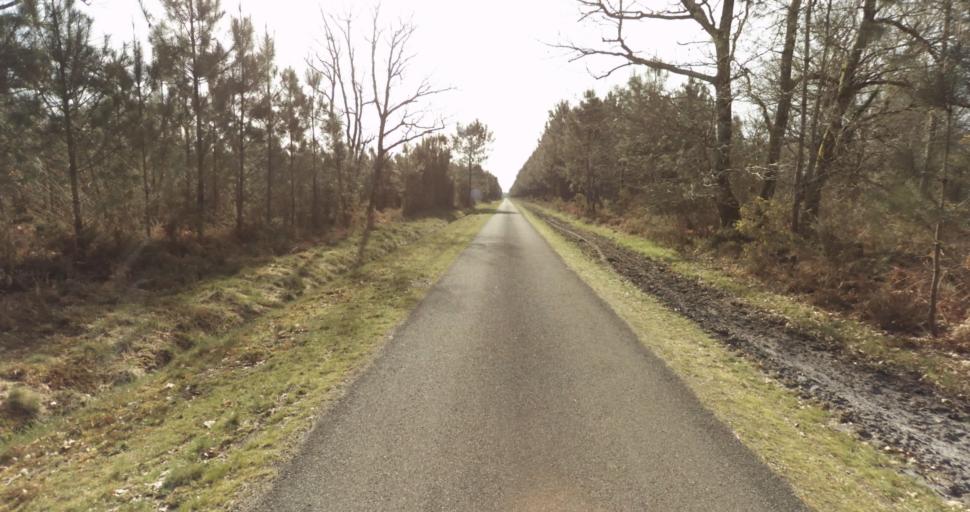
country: FR
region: Aquitaine
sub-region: Departement des Landes
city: Roquefort
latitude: 44.1324
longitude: -0.3193
